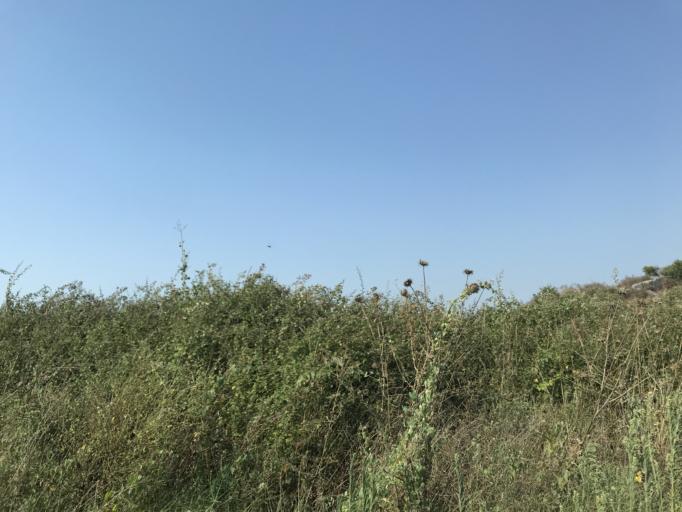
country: TR
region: Izmir
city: Selcuk
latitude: 37.9461
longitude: 27.3414
